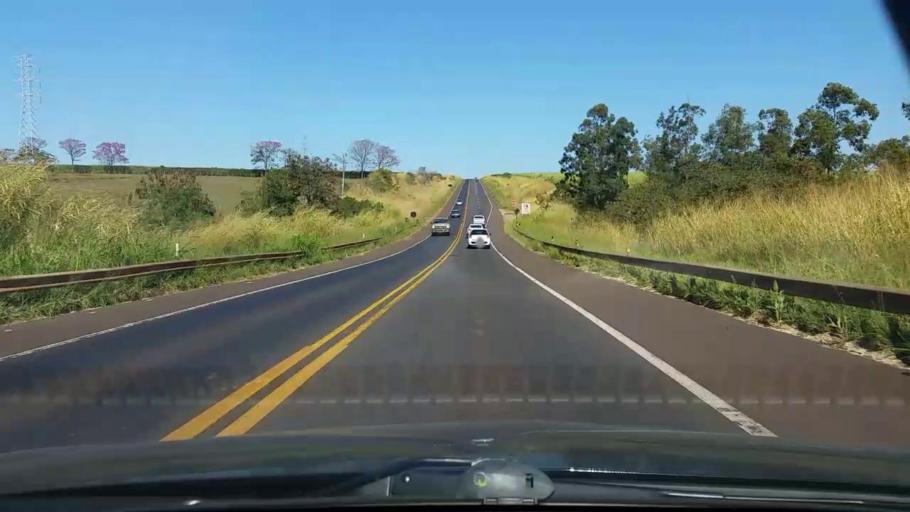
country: BR
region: Sao Paulo
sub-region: Jau
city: Jau
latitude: -22.3480
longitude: -48.5724
